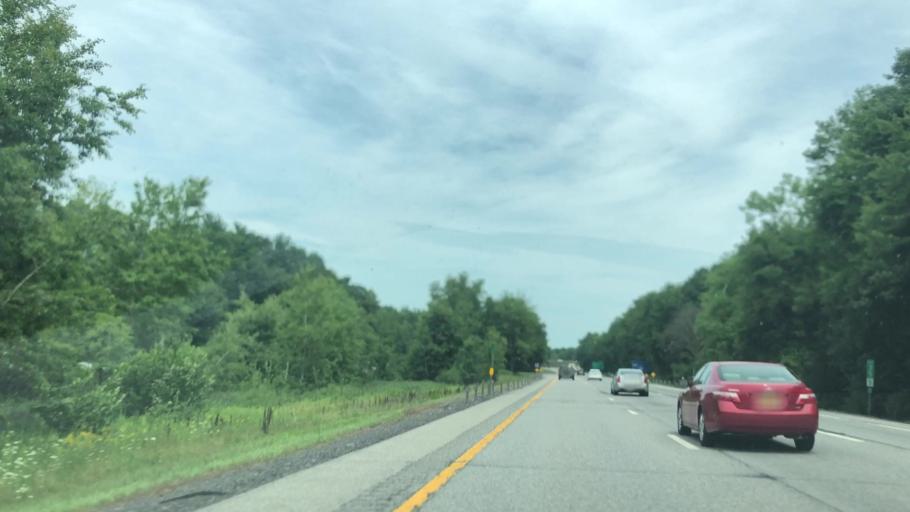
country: US
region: New York
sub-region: Saratoga County
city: Saratoga Springs
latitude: 43.1623
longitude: -73.7177
